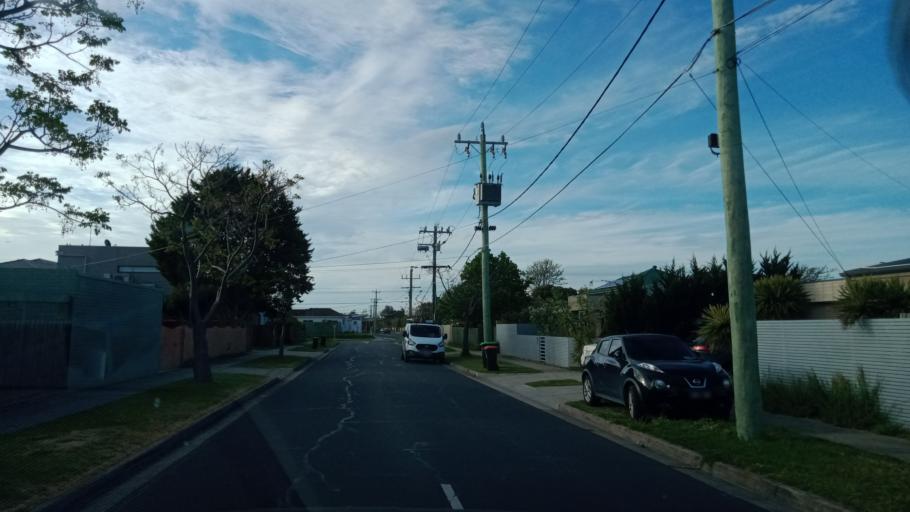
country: AU
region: Victoria
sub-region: Kingston
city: Chelsea
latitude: -38.0429
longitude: 145.1185
